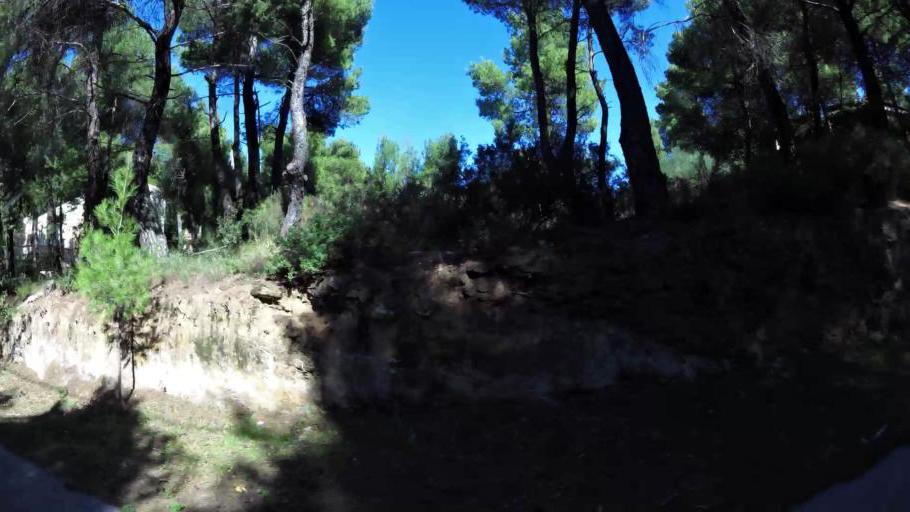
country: GR
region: Attica
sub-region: Nomarchia Anatolikis Attikis
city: Dionysos
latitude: 38.1026
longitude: 23.8888
